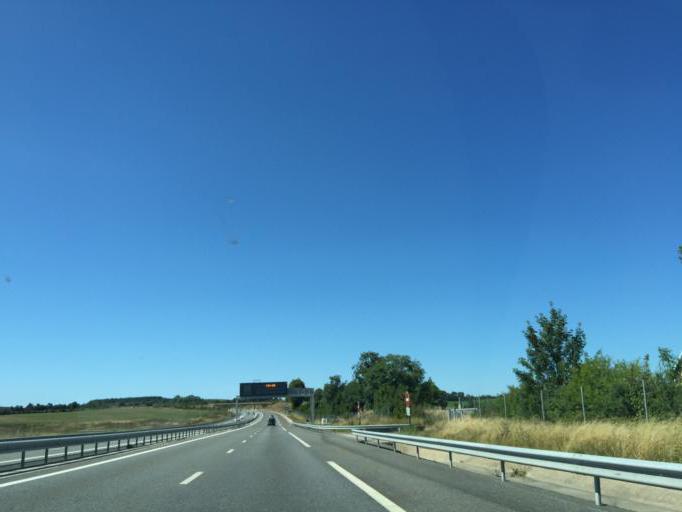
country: FR
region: Midi-Pyrenees
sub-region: Departement de l'Aveyron
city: La Cavalerie
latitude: 43.9906
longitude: 3.1769
